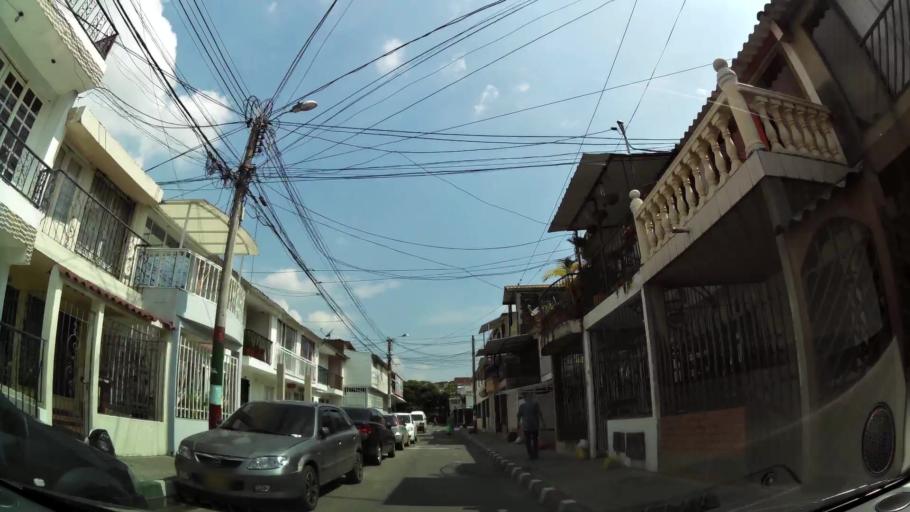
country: CO
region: Valle del Cauca
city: Cali
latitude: 3.4920
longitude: -76.5051
